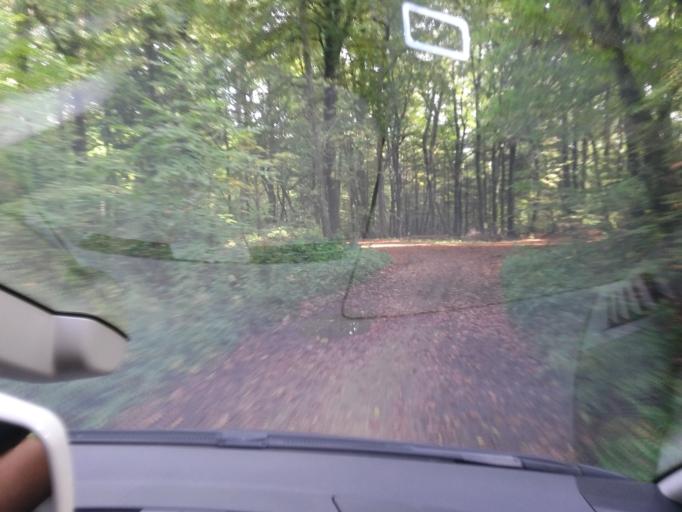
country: BE
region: Wallonia
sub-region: Province du Luxembourg
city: Attert
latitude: 49.7163
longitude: 5.7881
